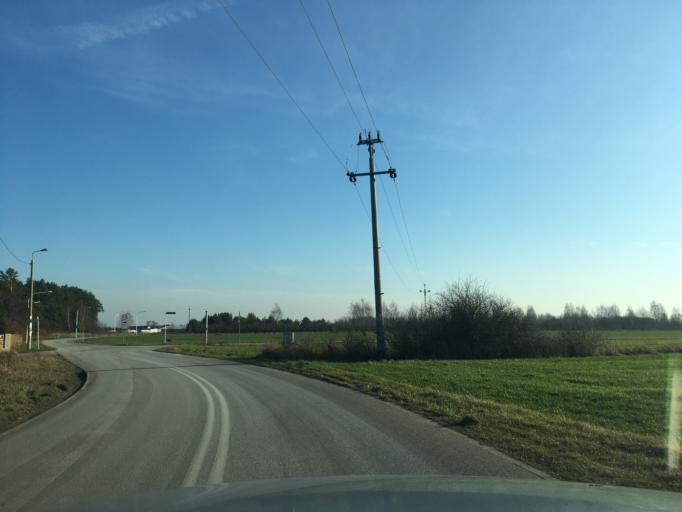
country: PL
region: Masovian Voivodeship
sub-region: Powiat pruszkowski
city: Nadarzyn
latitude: 52.0426
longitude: 20.8269
